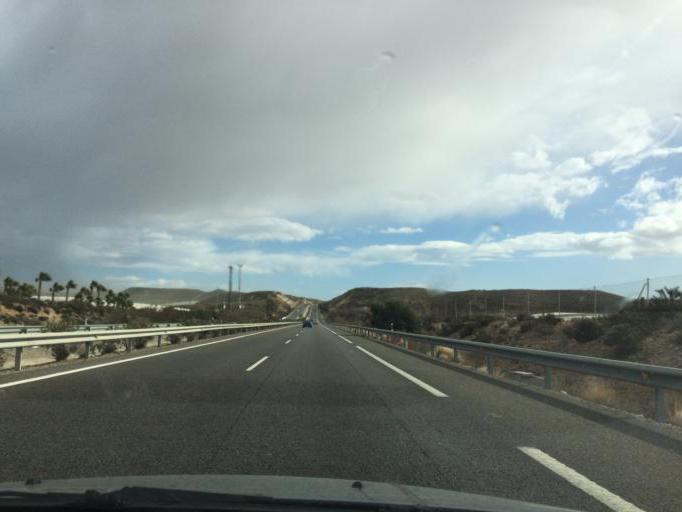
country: ES
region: Andalusia
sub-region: Provincia de Almeria
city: Retamar
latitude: 36.8699
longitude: -2.3011
